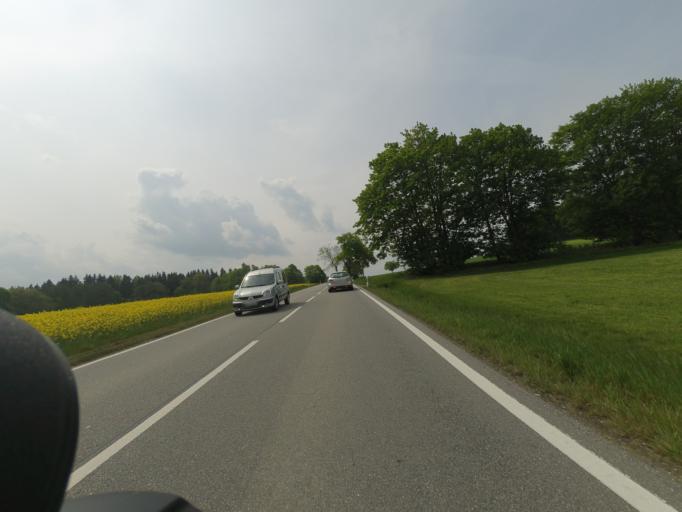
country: DE
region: Saxony
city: Olbernhau
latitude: 50.6515
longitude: 13.3058
